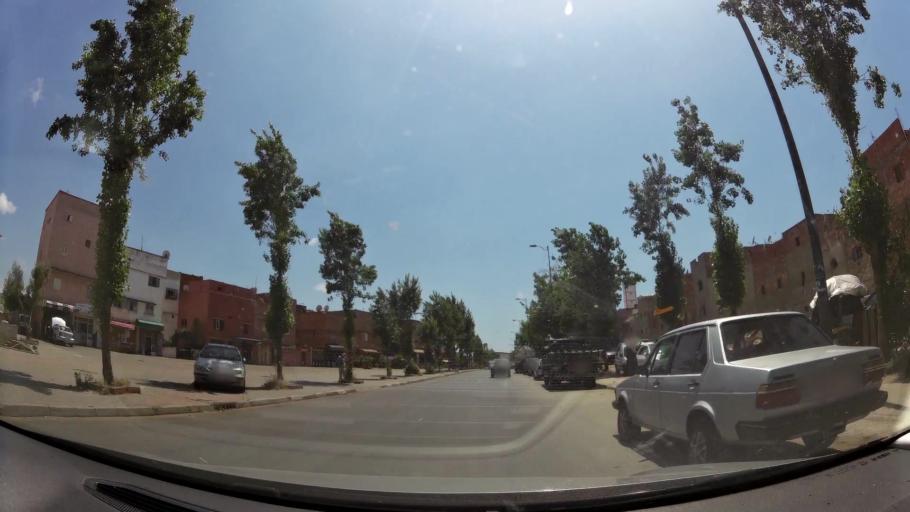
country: MA
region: Gharb-Chrarda-Beni Hssen
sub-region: Kenitra Province
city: Kenitra
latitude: 34.2512
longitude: -6.5522
